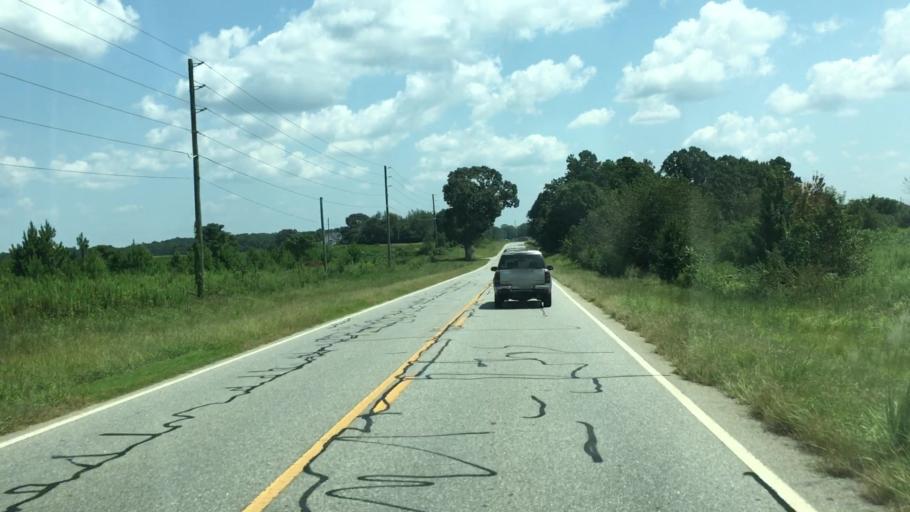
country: US
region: Georgia
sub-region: Barrow County
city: Statham
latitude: 33.9346
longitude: -83.6231
